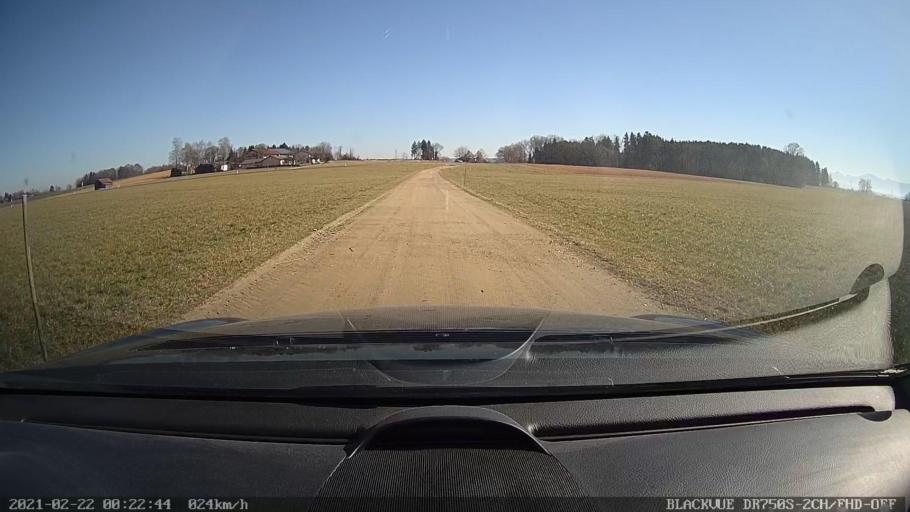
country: DE
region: Bavaria
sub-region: Upper Bavaria
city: Griesstatt
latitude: 47.9861
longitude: 12.1976
